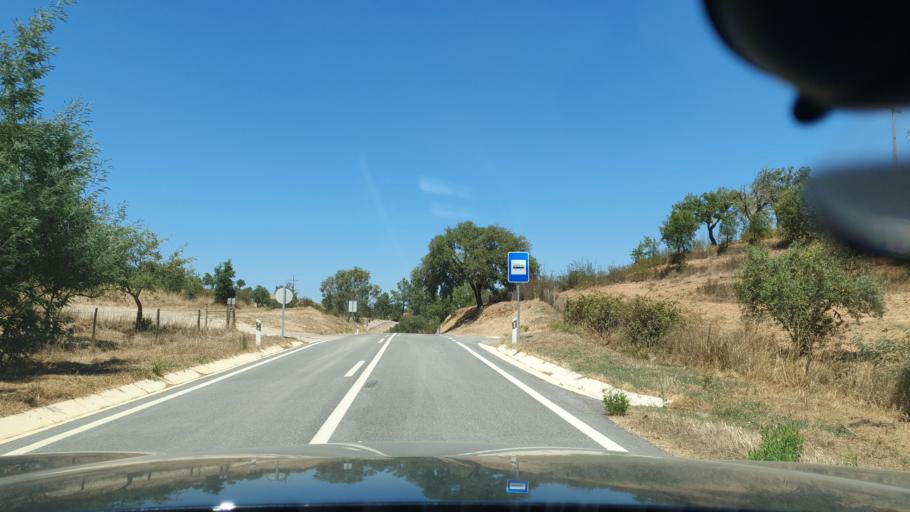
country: PT
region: Beja
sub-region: Odemira
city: Odemira
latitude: 37.5534
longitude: -8.4873
